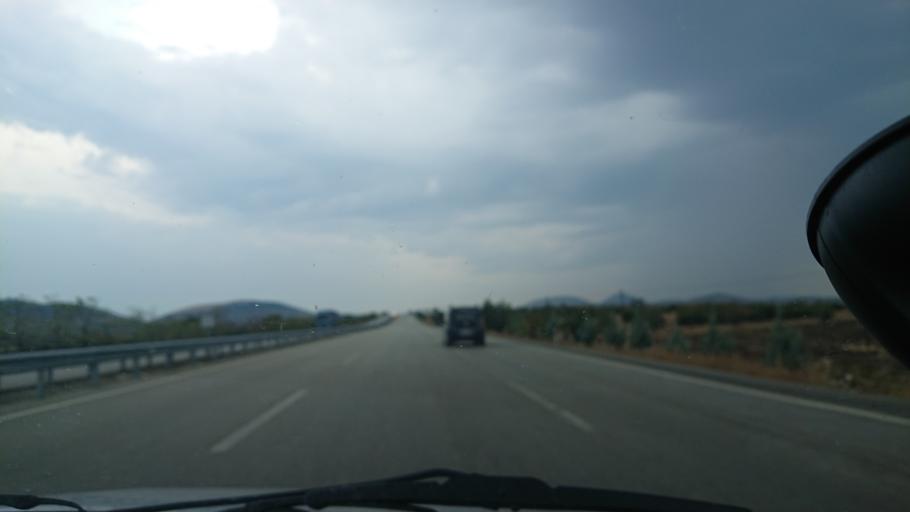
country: TR
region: Manisa
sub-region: Kula
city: Kula
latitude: 38.5705
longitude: 28.7333
